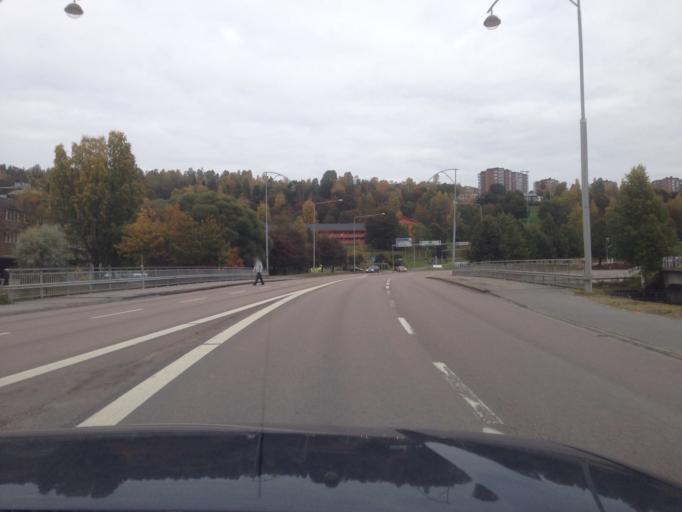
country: SE
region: Vaesternorrland
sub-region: Sundsvalls Kommun
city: Sundsvall
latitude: 62.3926
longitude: 17.3130
